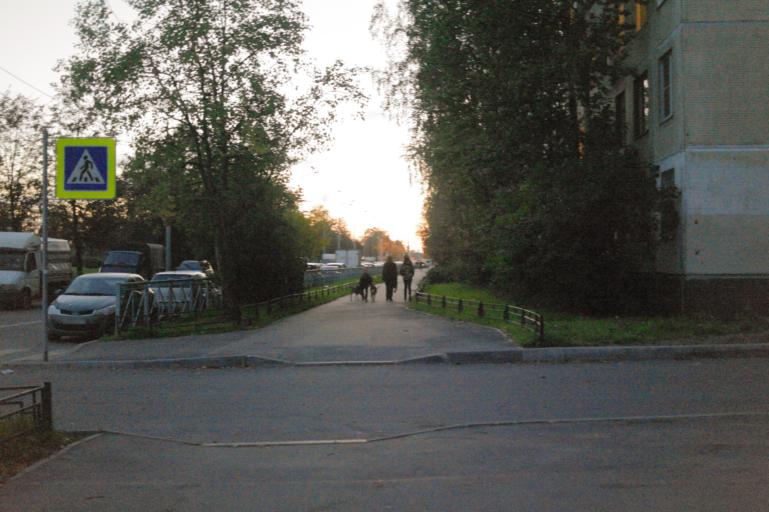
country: RU
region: St.-Petersburg
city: Obukhovo
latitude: 59.8991
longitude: 30.4796
